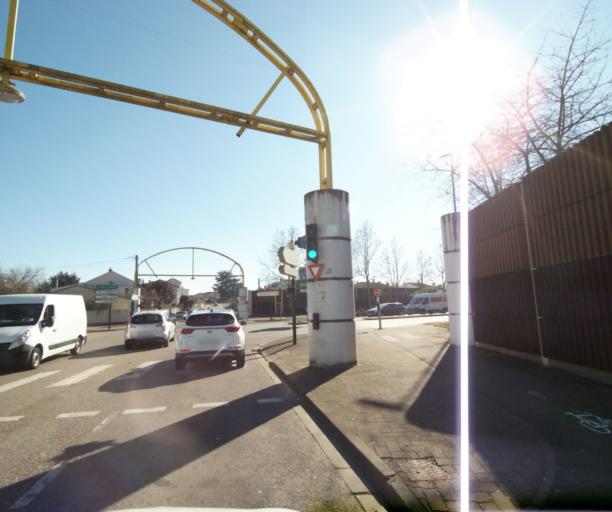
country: FR
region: Lorraine
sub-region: Departement de Meurthe-et-Moselle
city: Tomblaine
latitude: 48.6818
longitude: 6.2159
